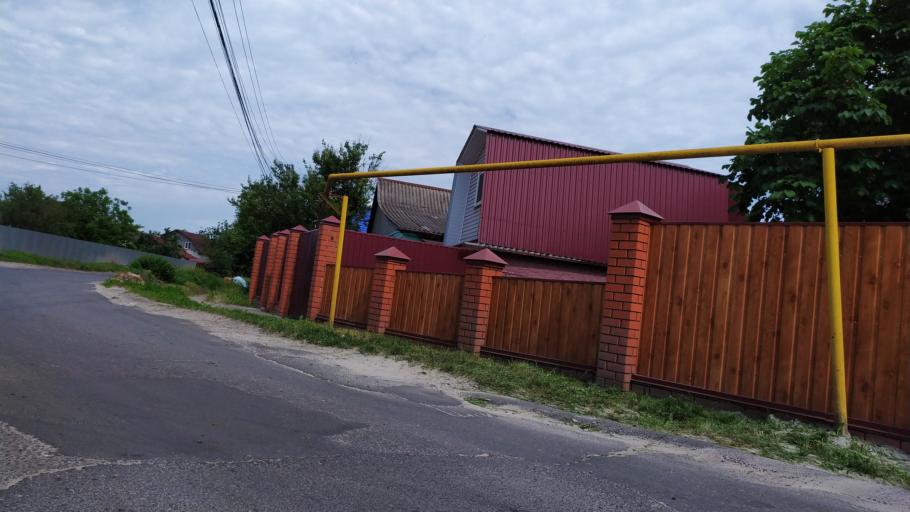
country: RU
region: Kursk
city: Kursk
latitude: 51.6612
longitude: 36.1534
